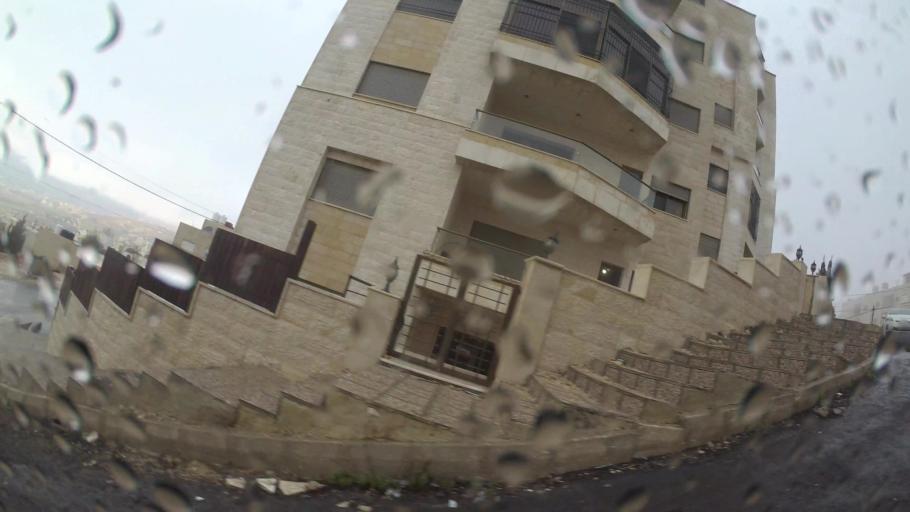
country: JO
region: Amman
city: Al Jubayhah
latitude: 32.0314
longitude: 35.8524
